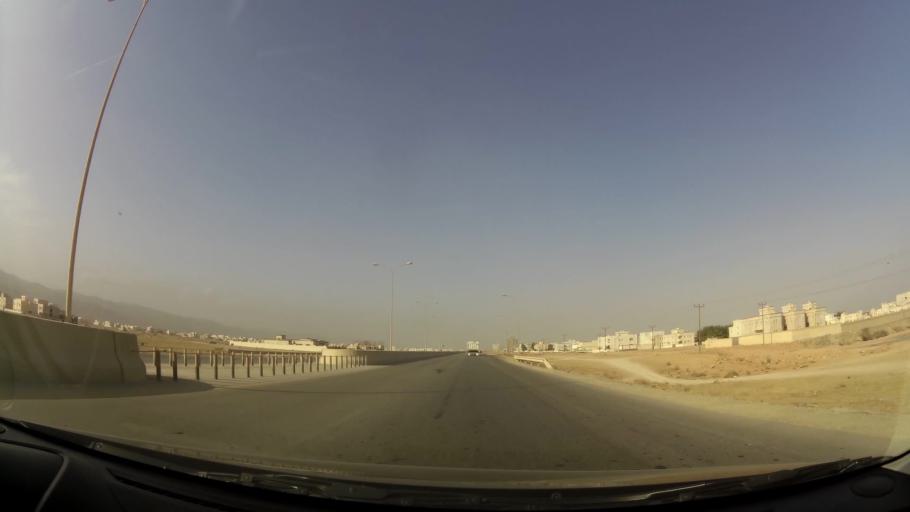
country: OM
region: Zufar
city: Salalah
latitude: 17.0212
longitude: 54.0152
